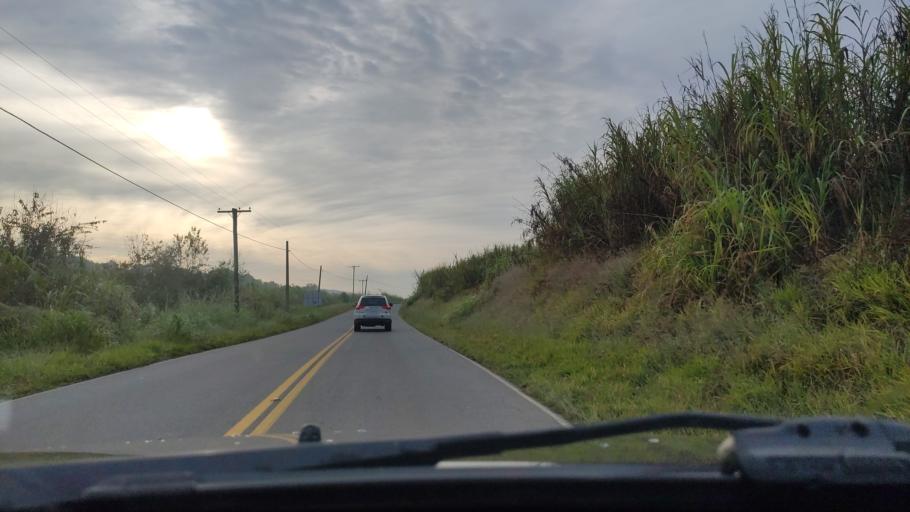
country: BR
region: Sao Paulo
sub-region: Campo Limpo Paulista
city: Campo Limpo Paulista
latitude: -23.1364
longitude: -46.7900
